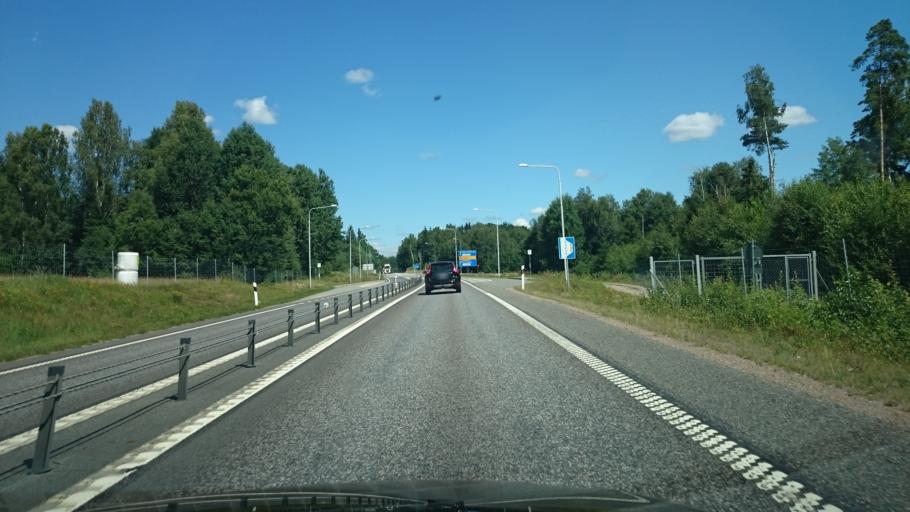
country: SE
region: Halland
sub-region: Hylte Kommun
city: Hyltebruk
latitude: 56.9864
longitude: 13.2151
